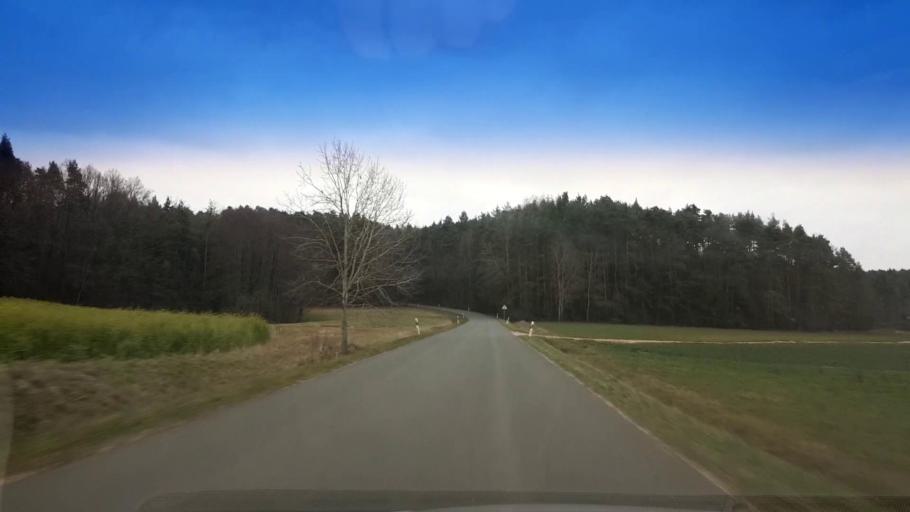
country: DE
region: Bavaria
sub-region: Upper Franconia
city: Pettstadt
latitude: 49.7732
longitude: 10.9166
